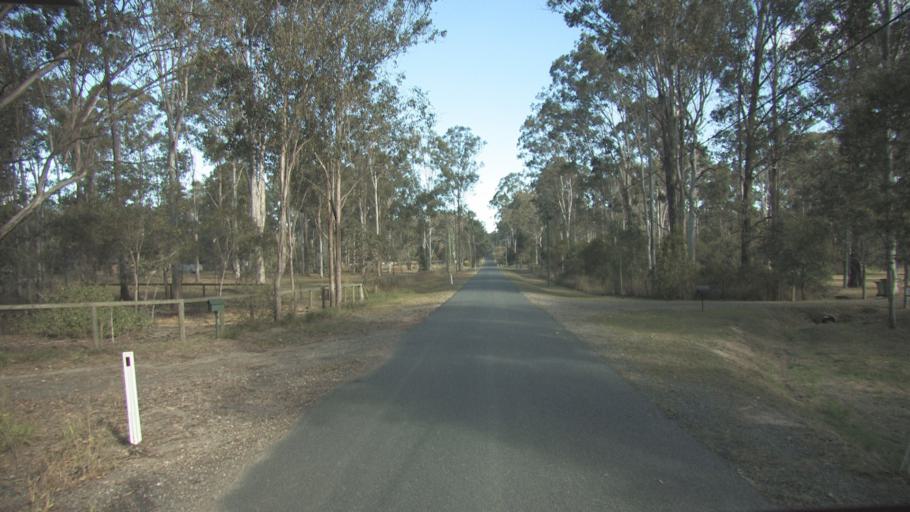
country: AU
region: Queensland
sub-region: Logan
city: North Maclean
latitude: -27.8231
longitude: 153.0631
